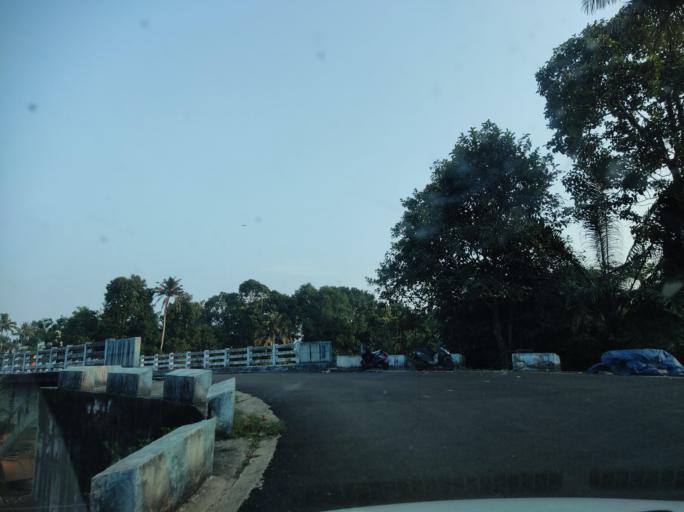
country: IN
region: Kerala
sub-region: Pattanamtitta
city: Tiruvalla
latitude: 9.3600
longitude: 76.5664
